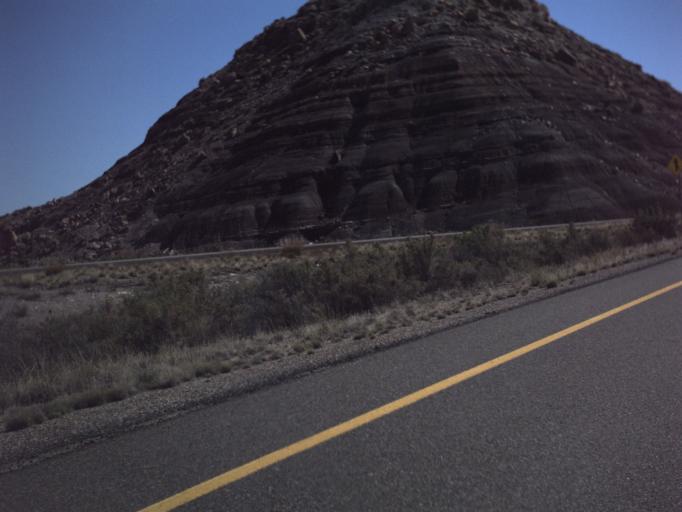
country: US
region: Utah
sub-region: Carbon County
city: East Carbon City
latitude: 38.9195
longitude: -110.3755
